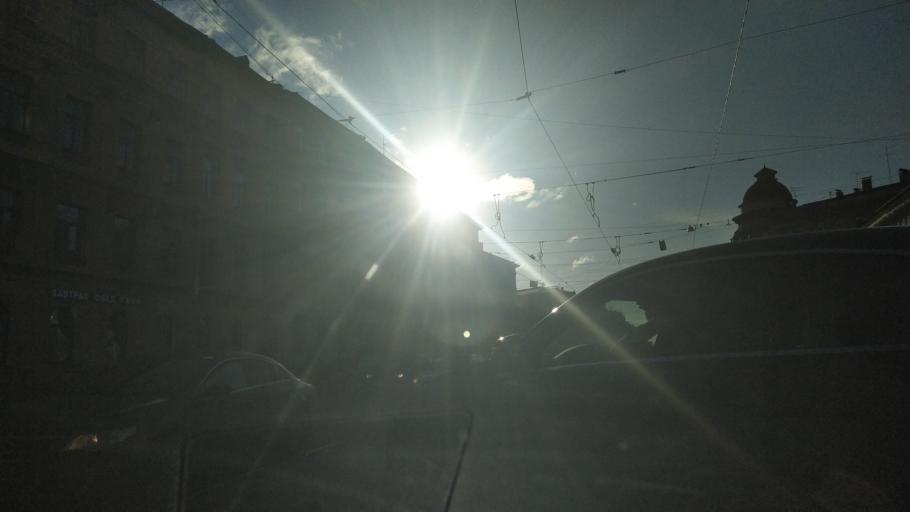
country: RU
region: St.-Petersburg
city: Centralniy
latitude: 59.9229
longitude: 30.3499
